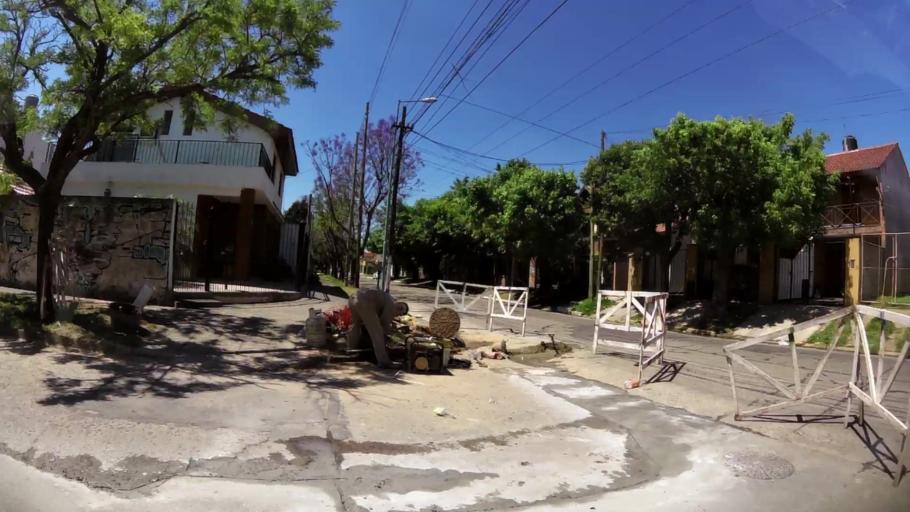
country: AR
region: Buenos Aires
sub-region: Partido de Merlo
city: Merlo
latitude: -34.6672
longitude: -58.6897
